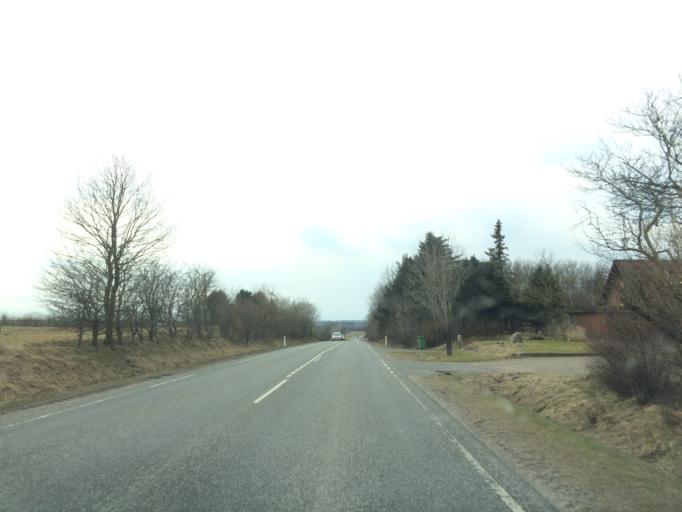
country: DK
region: Central Jutland
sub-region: Ringkobing-Skjern Kommune
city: Videbaek
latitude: 56.0806
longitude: 8.5071
